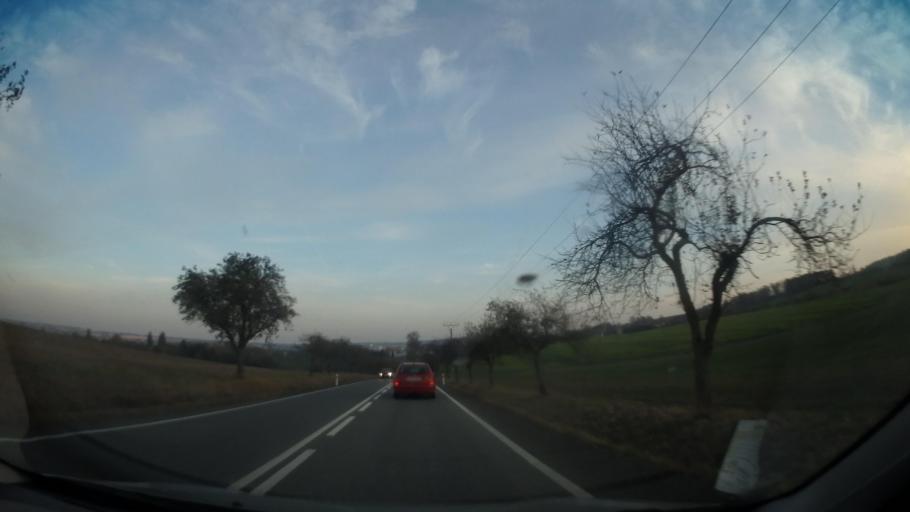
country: CZ
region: Central Bohemia
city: Cechtice
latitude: 49.6290
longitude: 15.0380
